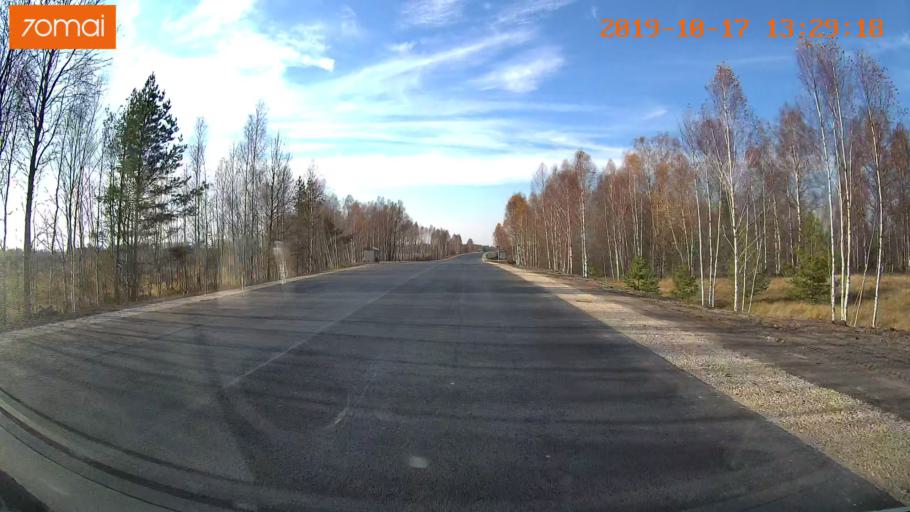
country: RU
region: Vladimir
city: Velikodvorskiy
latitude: 55.1190
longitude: 40.8445
